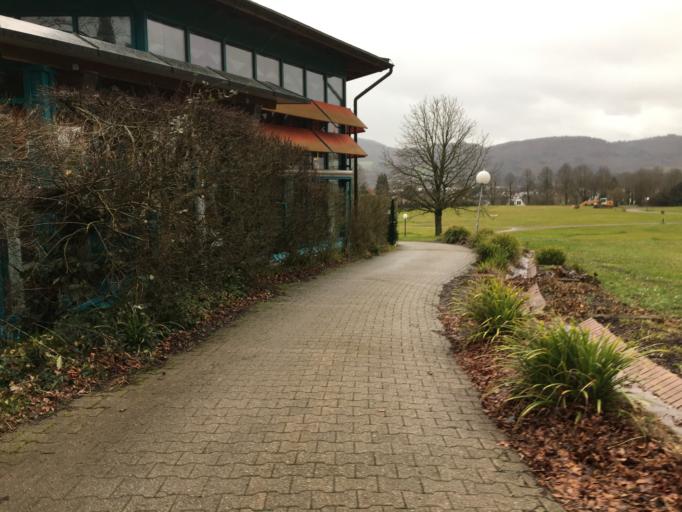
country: DE
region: Baden-Wuerttemberg
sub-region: Freiburg Region
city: Bad Sackingen
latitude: 47.5605
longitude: 7.9402
